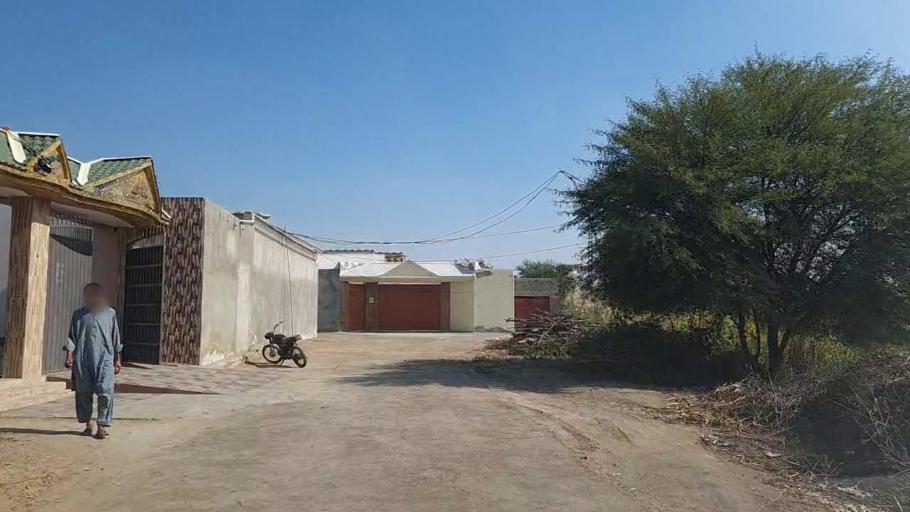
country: PK
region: Sindh
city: Bandhi
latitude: 26.5255
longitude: 68.3124
